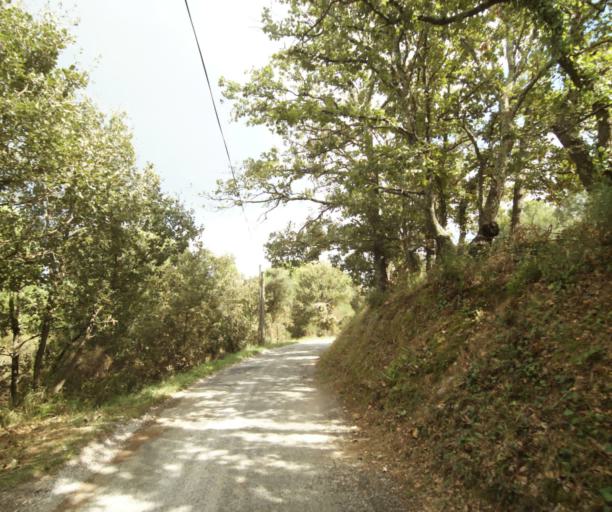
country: FR
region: Languedoc-Roussillon
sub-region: Departement des Pyrenees-Orientales
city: Argelers
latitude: 42.5403
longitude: 3.0127
